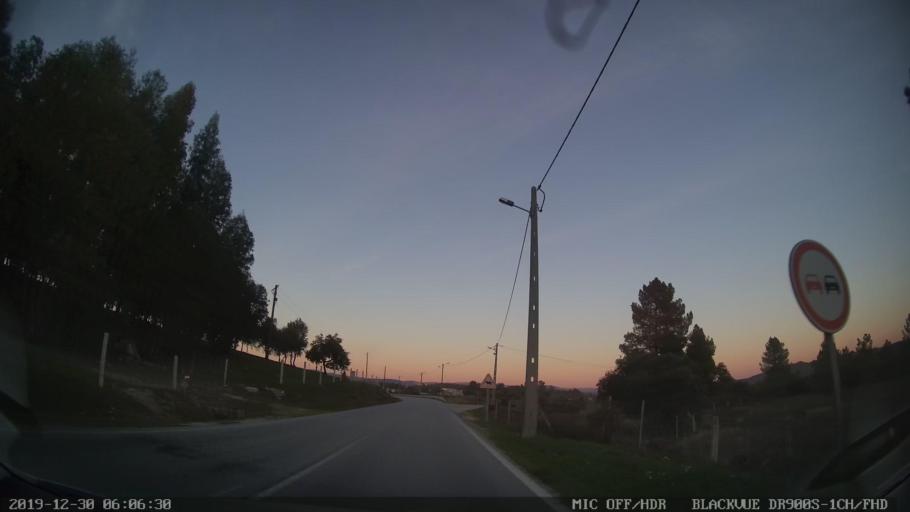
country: PT
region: Castelo Branco
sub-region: Penamacor
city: Penamacor
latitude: 40.0994
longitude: -7.2304
